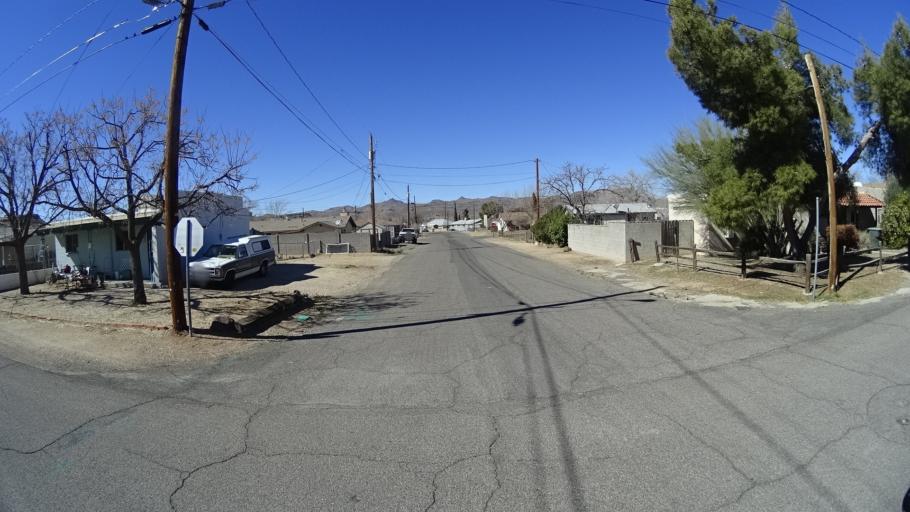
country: US
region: Arizona
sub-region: Mohave County
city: Kingman
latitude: 35.2018
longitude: -114.0274
